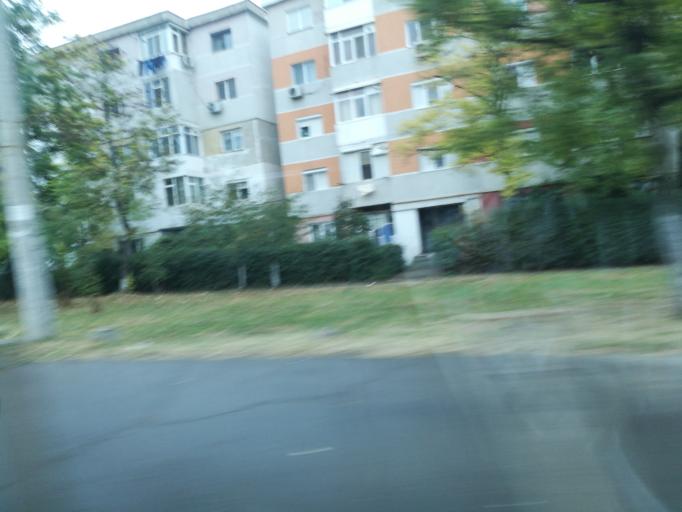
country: RO
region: Galati
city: Galati
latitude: 45.4529
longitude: 28.0141
